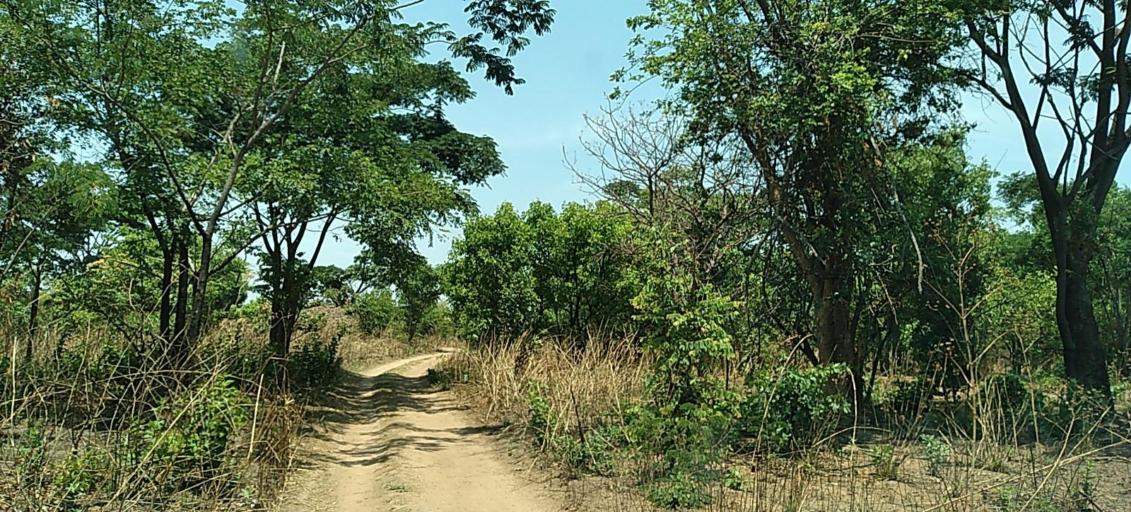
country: ZM
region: Copperbelt
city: Luanshya
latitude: -13.0654
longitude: 28.4052
